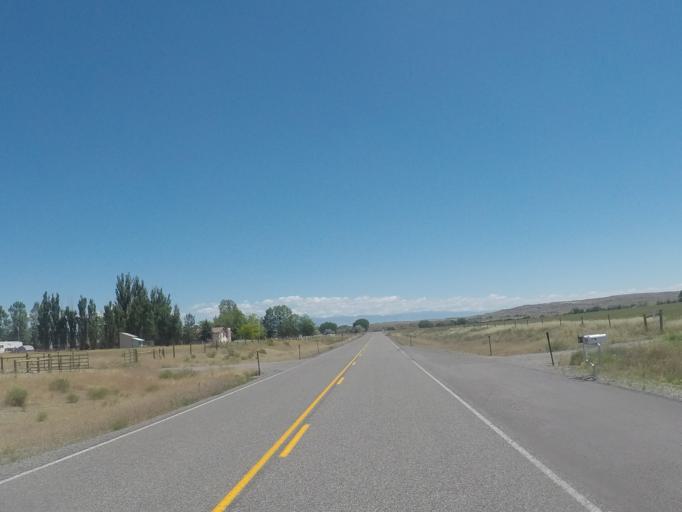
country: US
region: Wyoming
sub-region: Big Horn County
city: Lovell
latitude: 44.7674
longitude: -108.5367
